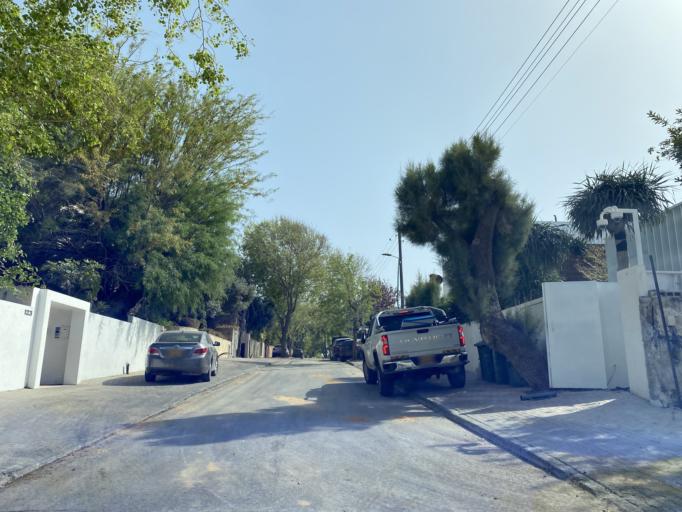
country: IL
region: Tel Aviv
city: Herzliya Pituah
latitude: 32.1770
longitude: 34.8073
